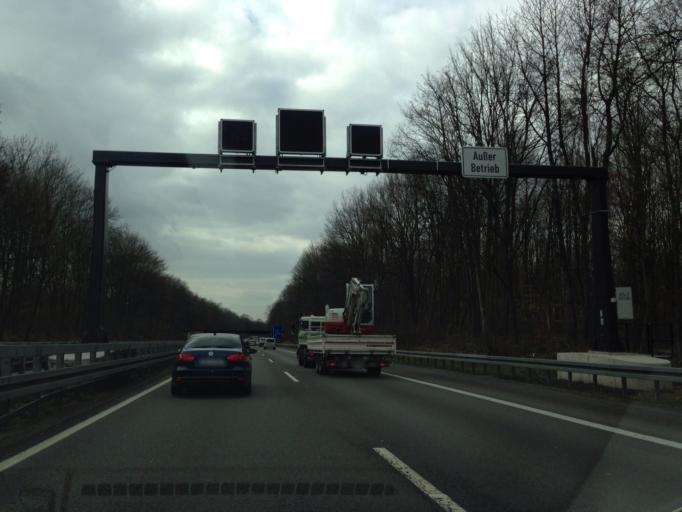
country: DE
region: North Rhine-Westphalia
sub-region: Regierungsbezirk Arnsberg
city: Herne
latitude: 51.5107
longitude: 7.2284
